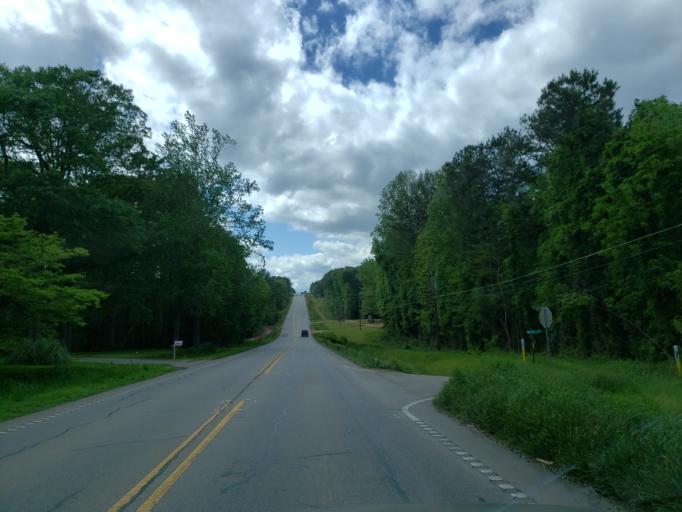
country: US
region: Georgia
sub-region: Haralson County
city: Bremen
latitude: 33.7103
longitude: -85.2061
